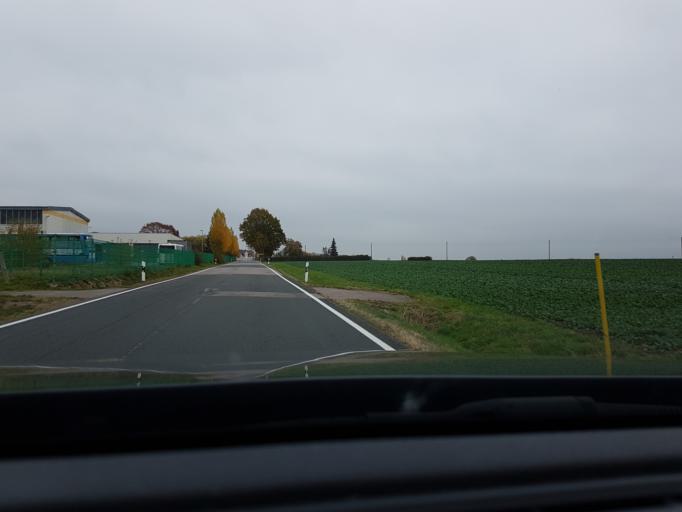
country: DE
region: Saxony
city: Altmittweida
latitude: 50.9846
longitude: 12.9430
